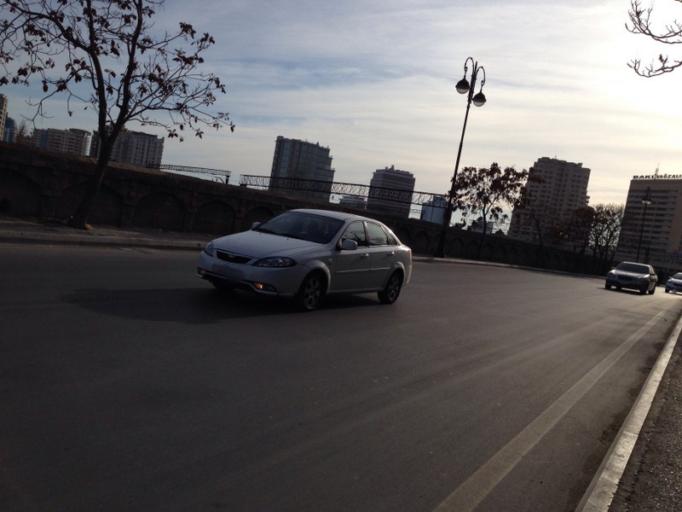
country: AZ
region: Baki
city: Baku
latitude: 40.3828
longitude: 49.8516
